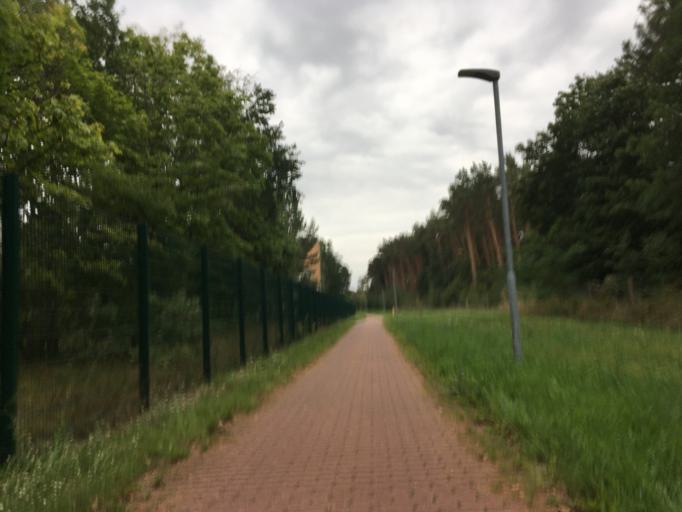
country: DE
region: Brandenburg
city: Meyenburg
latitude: 53.0851
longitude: 14.2316
